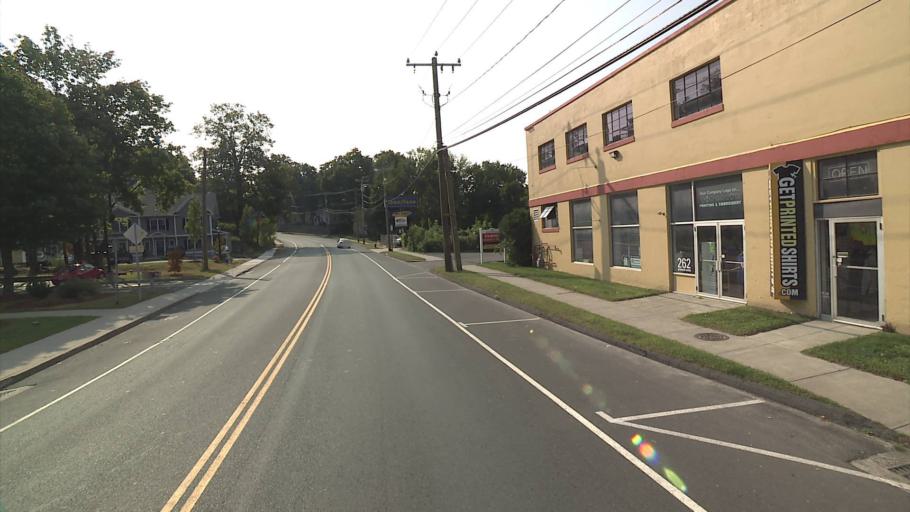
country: US
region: Connecticut
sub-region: Fairfield County
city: Bethel
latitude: 41.3735
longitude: -73.4220
